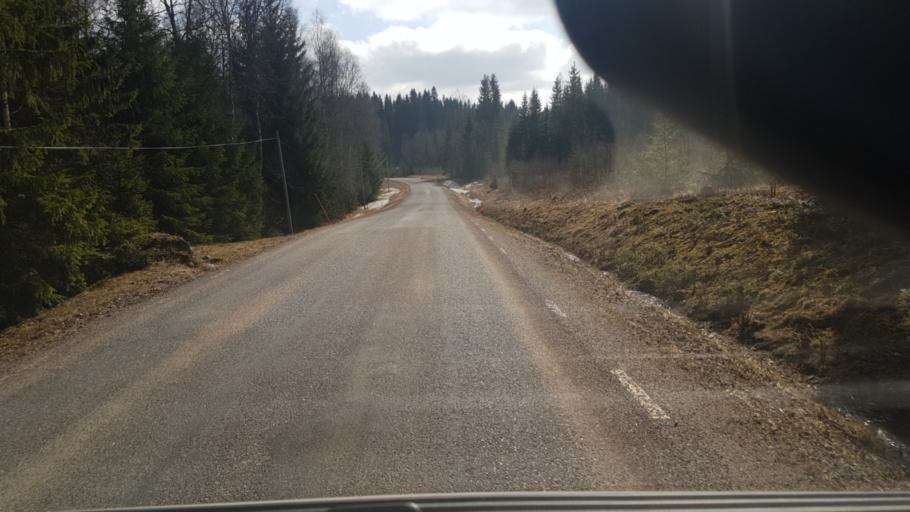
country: SE
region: Vaermland
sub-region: Eda Kommun
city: Amotfors
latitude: 59.8524
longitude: 12.4252
